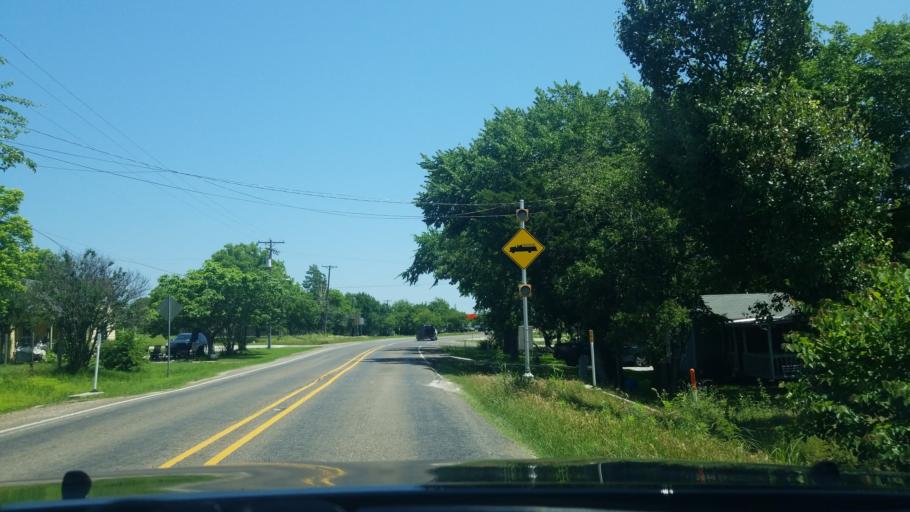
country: US
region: Texas
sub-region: Denton County
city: Krum
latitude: 33.2636
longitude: -97.2372
